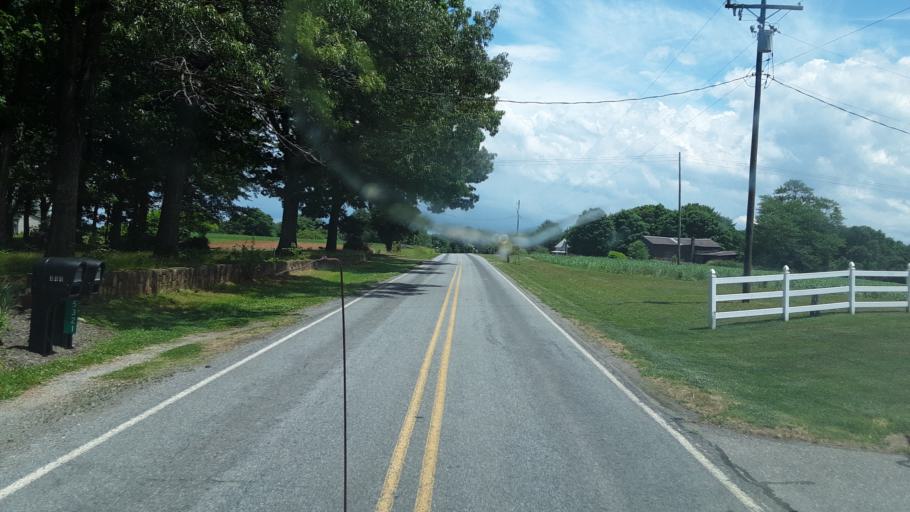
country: US
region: North Carolina
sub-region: Yadkin County
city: Jonesville
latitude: 36.0734
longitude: -80.8416
